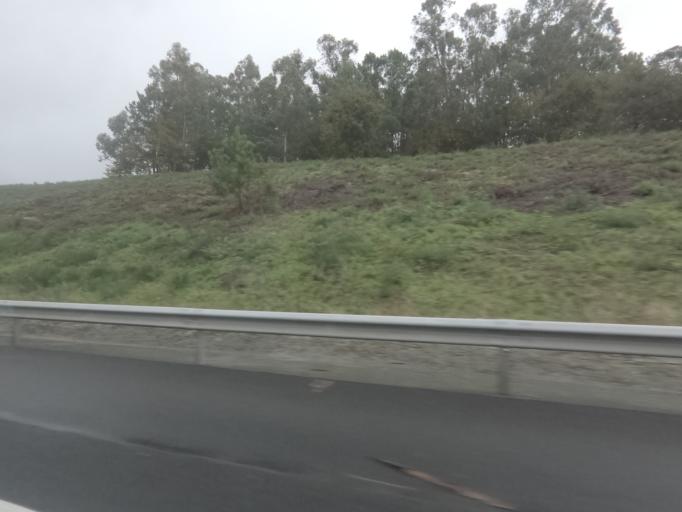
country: ES
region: Galicia
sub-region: Provincia de Pontevedra
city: Vigo
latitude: 42.2397
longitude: -8.6580
